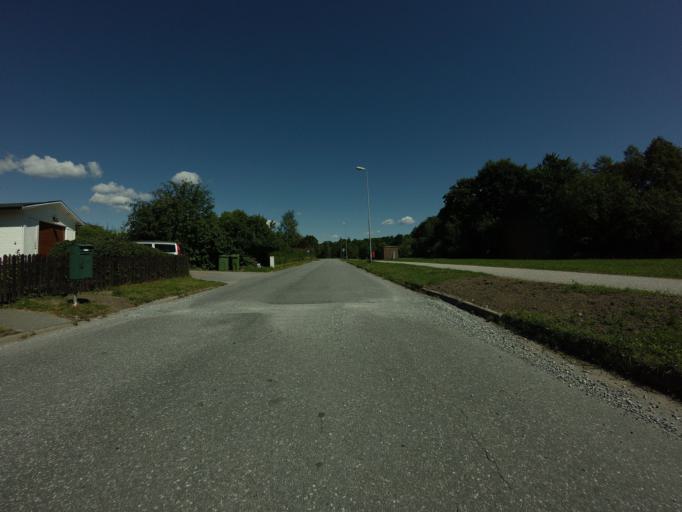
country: SE
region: Stockholm
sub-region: Sollentuna Kommun
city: Sollentuna
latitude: 59.4555
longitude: 17.9017
